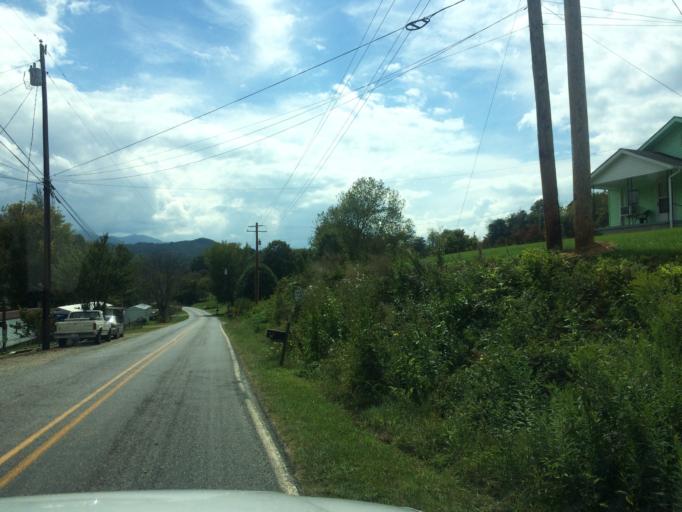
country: US
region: North Carolina
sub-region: Haywood County
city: Clyde
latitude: 35.5409
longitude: -82.9153
